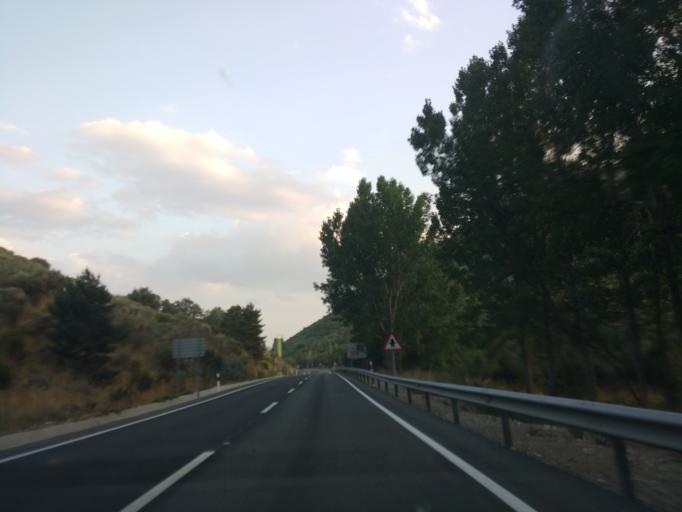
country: ES
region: Castille and Leon
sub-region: Provincia de Avila
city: Hoyos de Miguel Munoz
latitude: 40.4084
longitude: -5.0314
